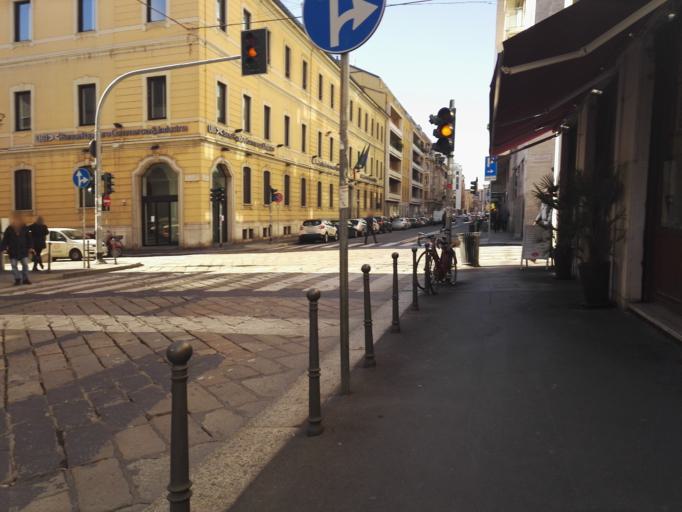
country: IT
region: Lombardy
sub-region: Citta metropolitana di Milano
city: Milano
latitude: 45.4770
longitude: 9.1882
